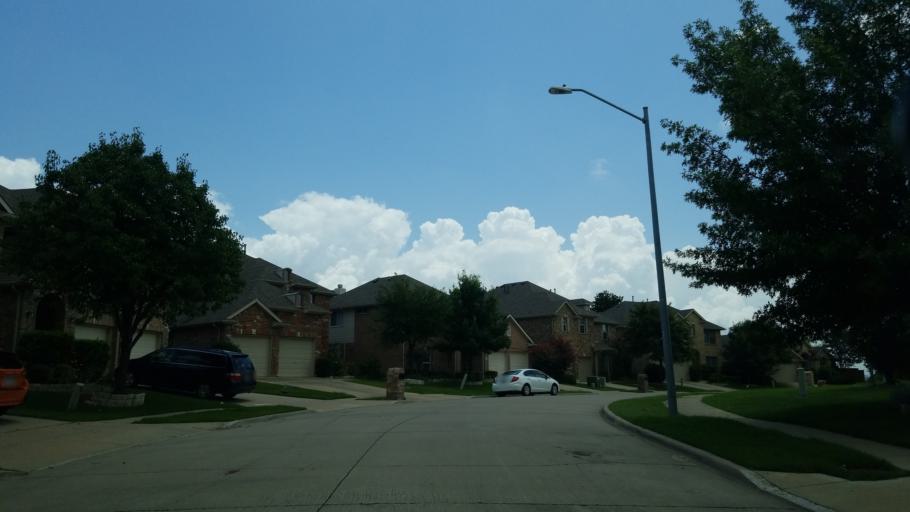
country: US
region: Texas
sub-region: Dallas County
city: Coppell
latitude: 32.9447
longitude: -96.9603
